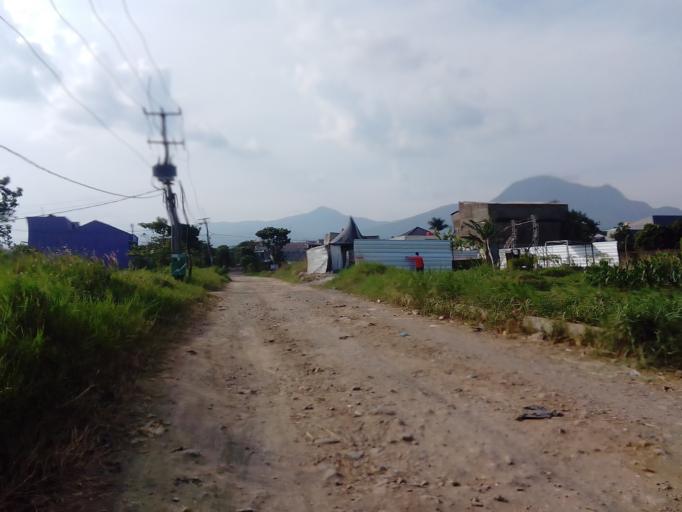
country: ID
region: West Java
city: Cileunyi
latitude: -6.9342
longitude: 107.7135
